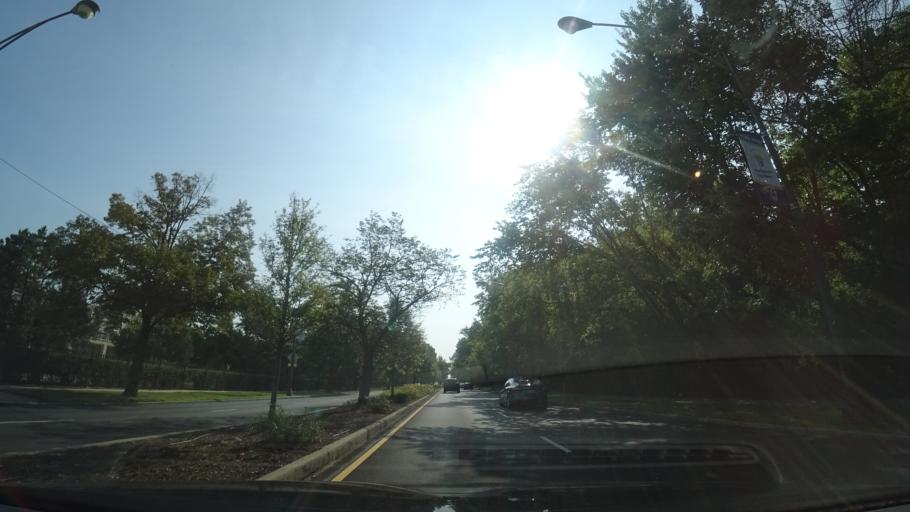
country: US
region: Illinois
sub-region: Cook County
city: Lincolnwood
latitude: 41.9902
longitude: -87.7276
